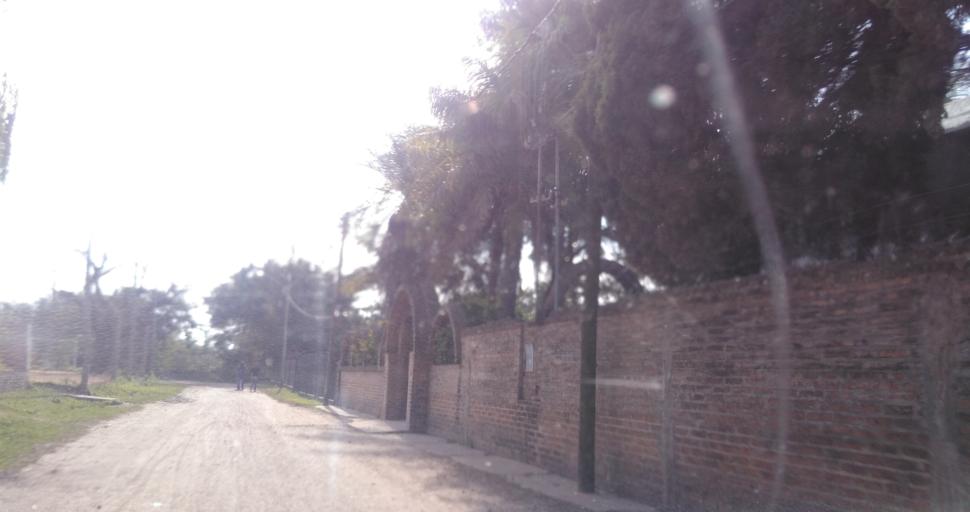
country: AR
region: Chaco
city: Fontana
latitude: -27.4265
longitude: -59.0118
